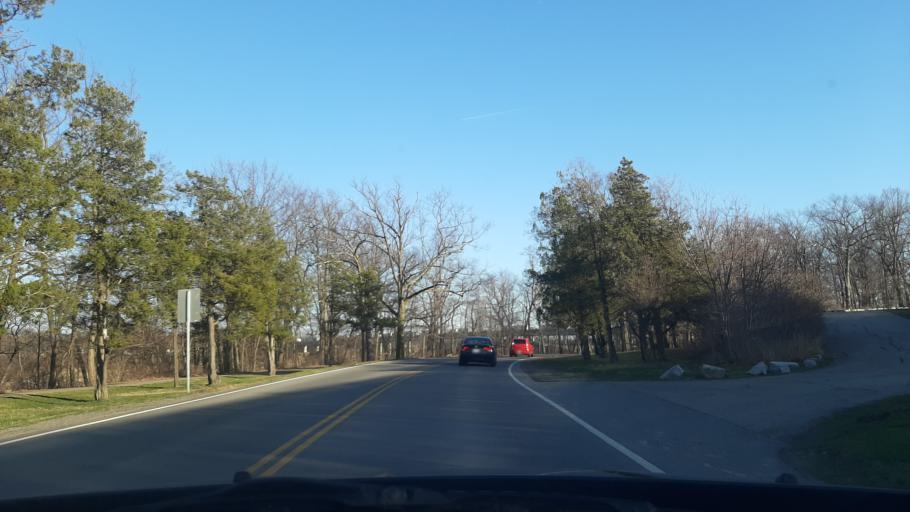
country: US
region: New York
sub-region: Niagara County
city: Lewiston
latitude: 43.1561
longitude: -79.0480
